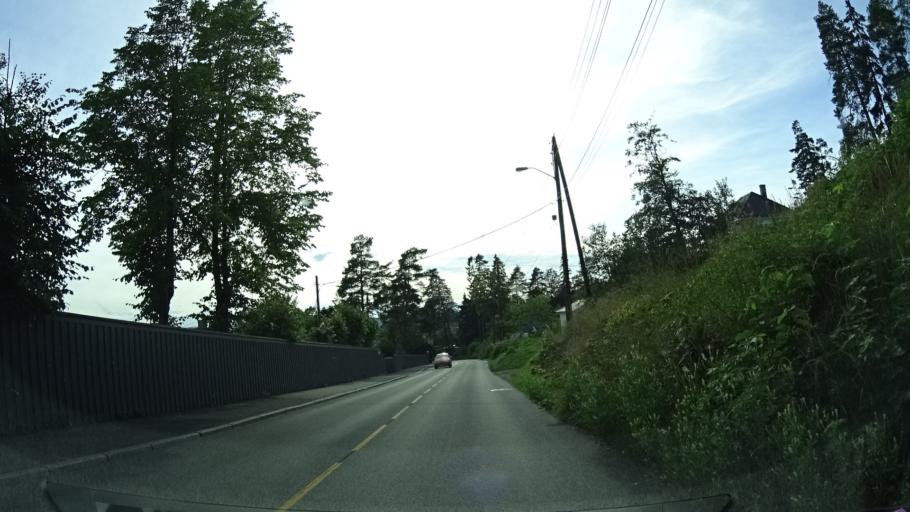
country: NO
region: Oslo
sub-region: Oslo
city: Sjolyststranda
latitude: 59.9568
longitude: 10.6713
